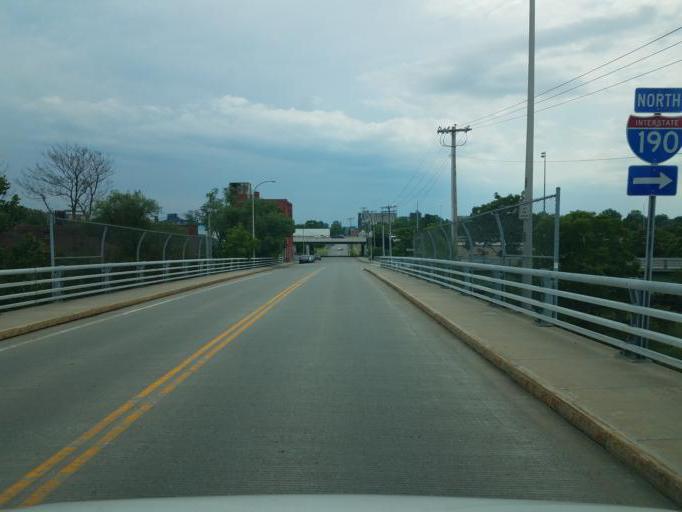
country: US
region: New York
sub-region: Erie County
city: Buffalo
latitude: 42.8752
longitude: -78.8569
